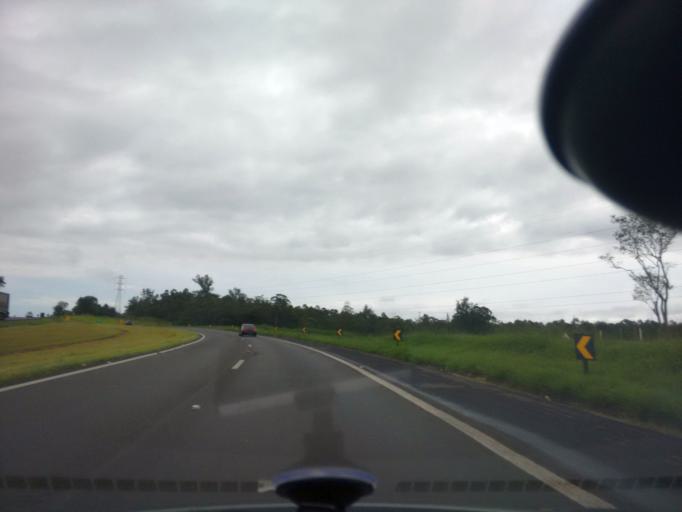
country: BR
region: Sao Paulo
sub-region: Rio Claro
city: Rio Claro
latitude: -22.3142
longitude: -47.6619
